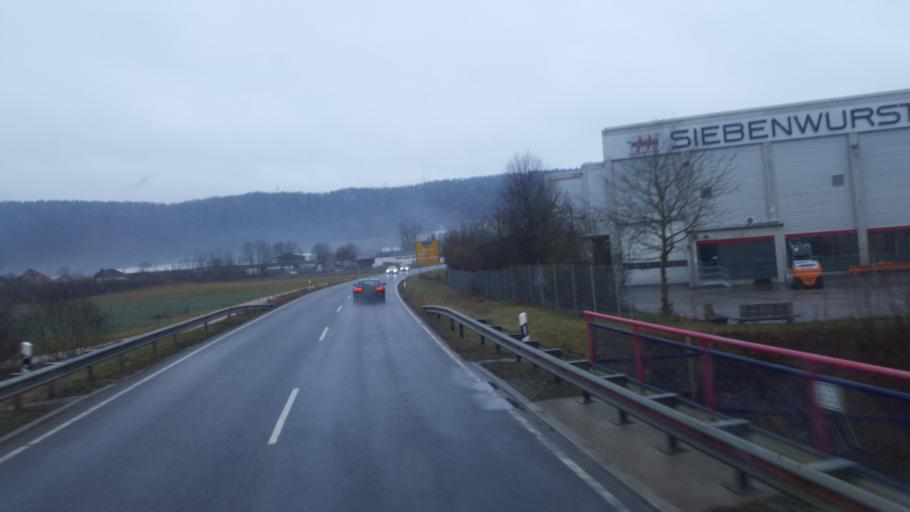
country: DE
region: Bavaria
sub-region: Upper Palatinate
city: Dietfurt
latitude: 49.0286
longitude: 11.5944
